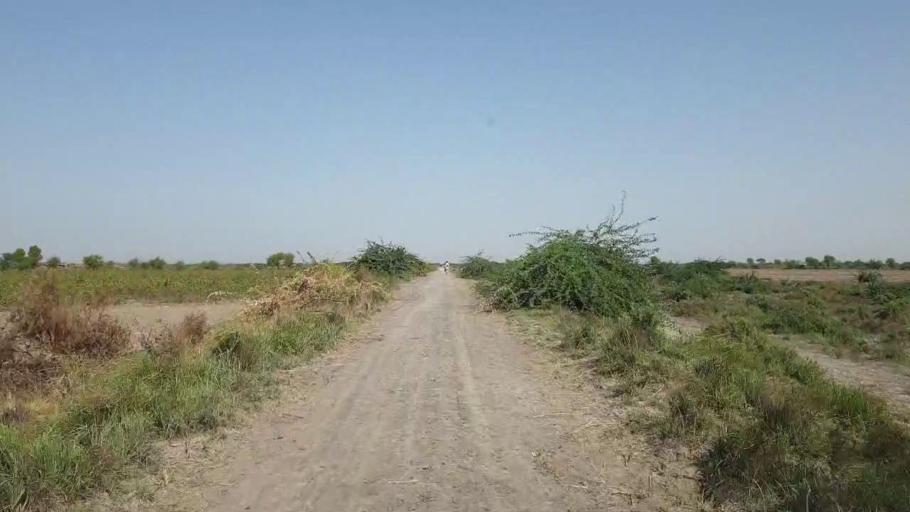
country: PK
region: Sindh
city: Tando Bago
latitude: 24.7042
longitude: 69.0710
